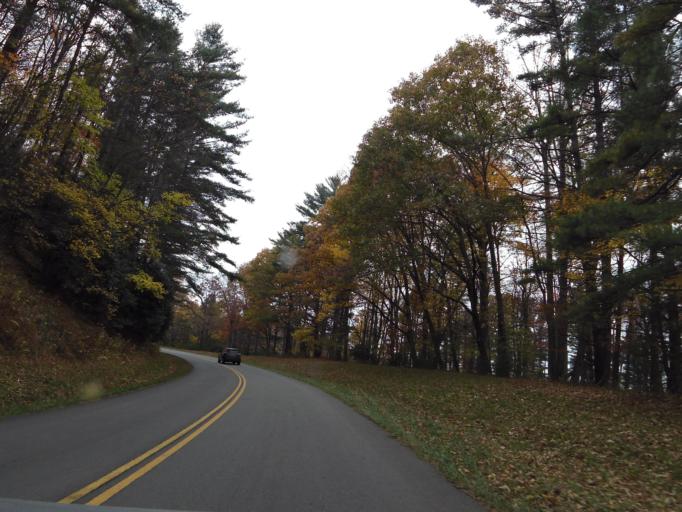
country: US
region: North Carolina
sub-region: Wilkes County
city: Mulberry
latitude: 36.3709
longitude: -81.2973
